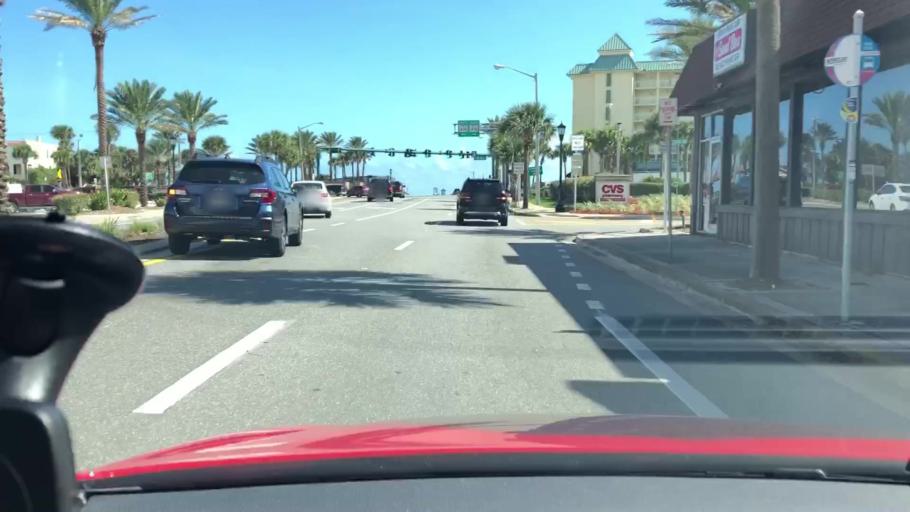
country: US
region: Florida
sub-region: Volusia County
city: Ormond Beach
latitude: 29.2915
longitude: -81.0409
